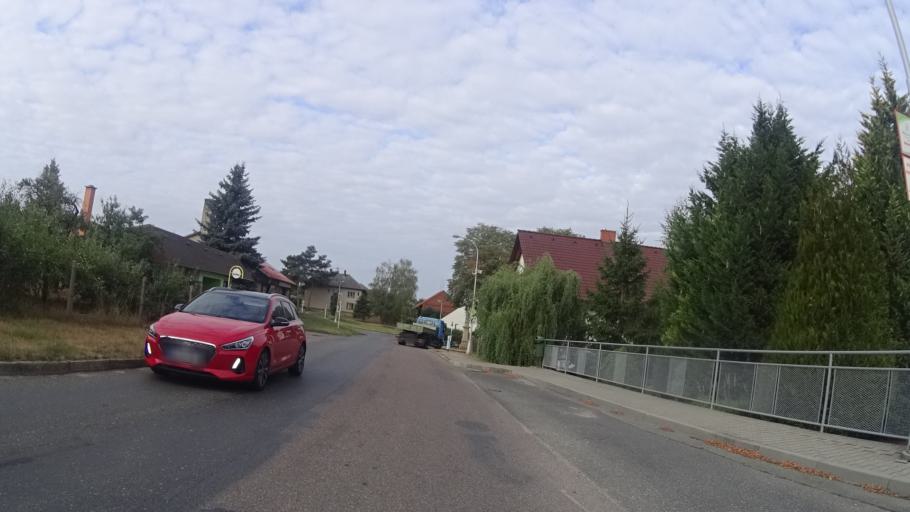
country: CZ
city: Stezery
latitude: 50.2083
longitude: 15.7121
